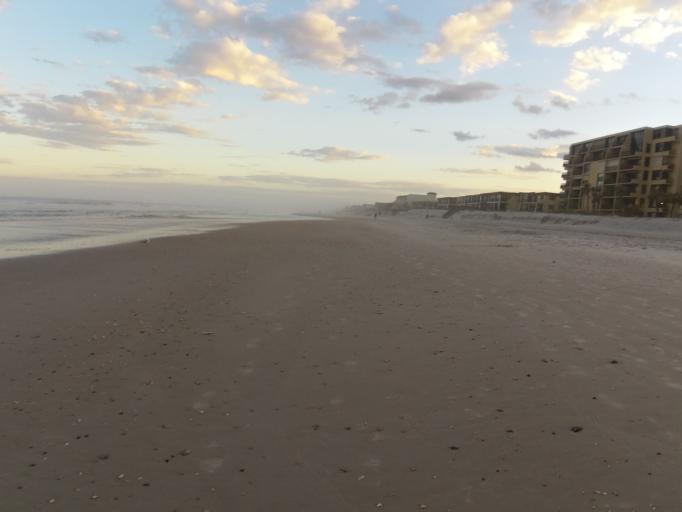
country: US
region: Florida
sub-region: Duval County
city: Jacksonville Beach
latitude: 30.2710
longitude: -81.3843
